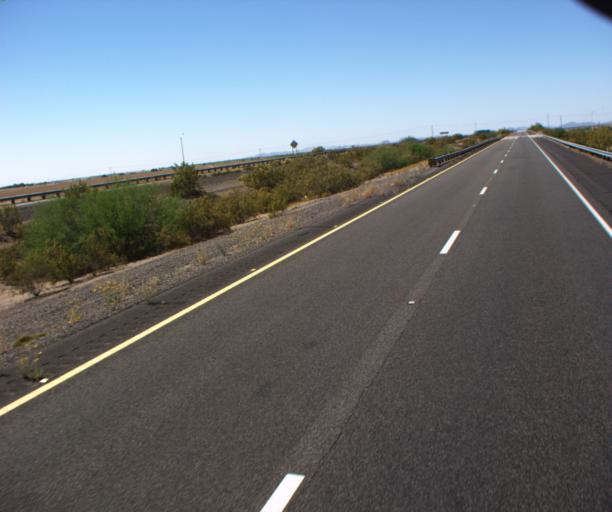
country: US
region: Arizona
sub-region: Maricopa County
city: Gila Bend
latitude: 32.9398
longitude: -112.7321
